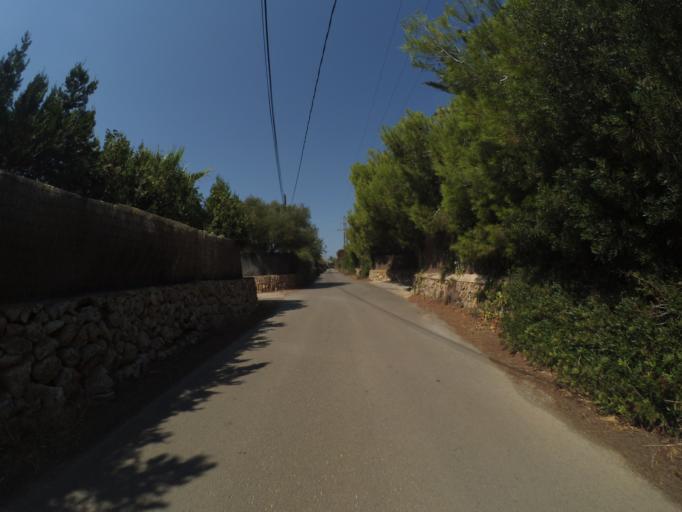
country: ES
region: Balearic Islands
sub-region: Illes Balears
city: Santanyi
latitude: 39.3903
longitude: 3.2385
